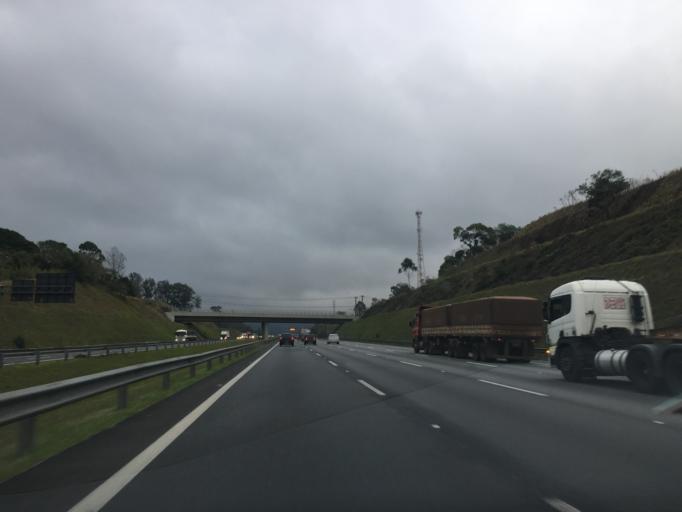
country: BR
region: Sao Paulo
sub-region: Caieiras
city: Caieiras
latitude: -23.4378
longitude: -46.7669
